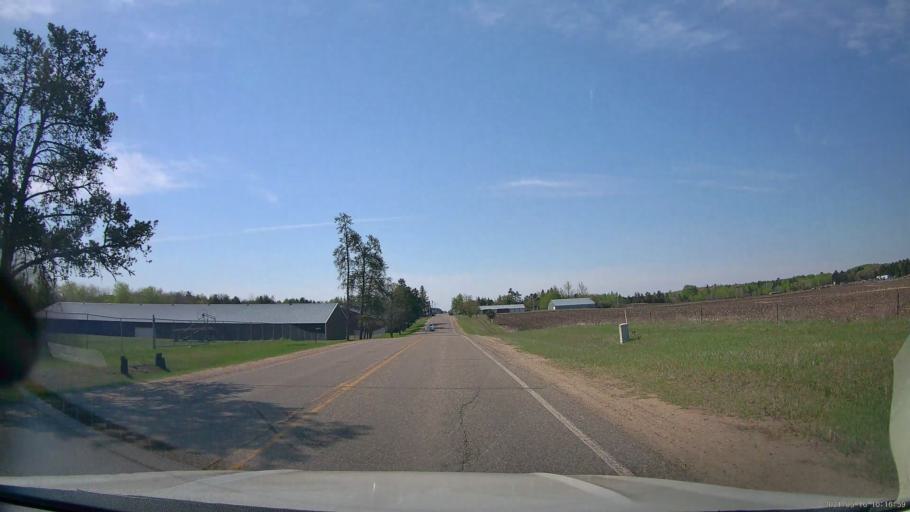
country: US
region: Minnesota
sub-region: Hubbard County
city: Park Rapids
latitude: 46.9601
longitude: -94.9527
